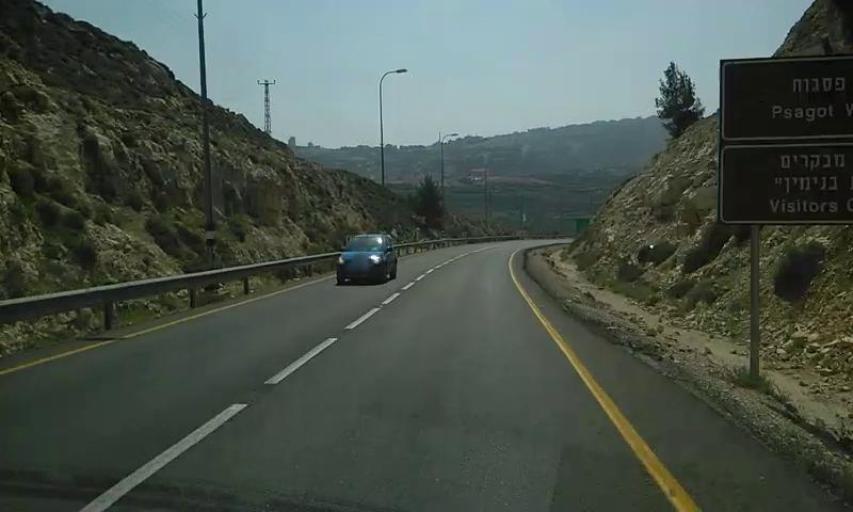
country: PS
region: West Bank
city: Mikhmas
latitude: 31.8741
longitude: 35.2642
